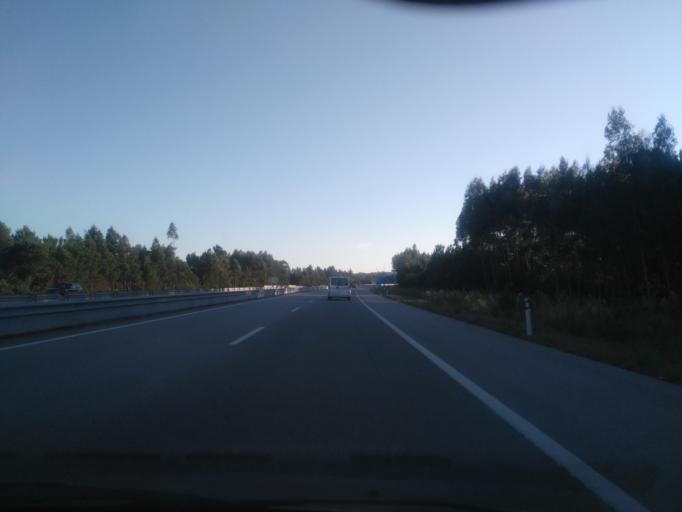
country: PT
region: Coimbra
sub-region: Figueira da Foz
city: Alhadas
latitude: 40.2289
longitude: -8.7899
